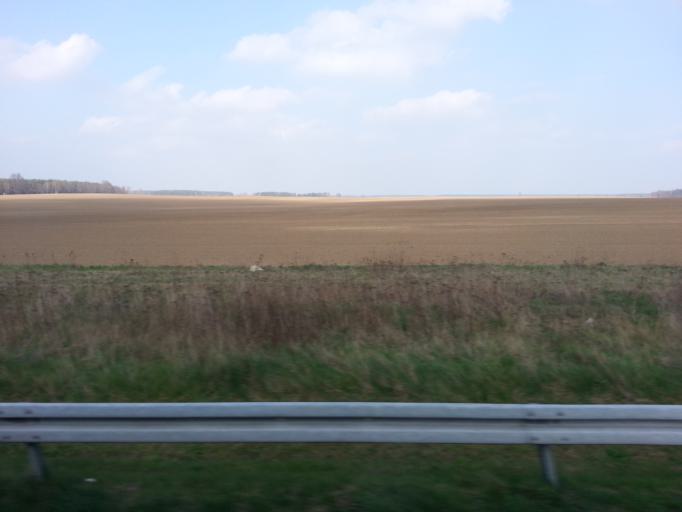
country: DE
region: Brandenburg
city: Walsleben
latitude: 52.9973
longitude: 12.6037
